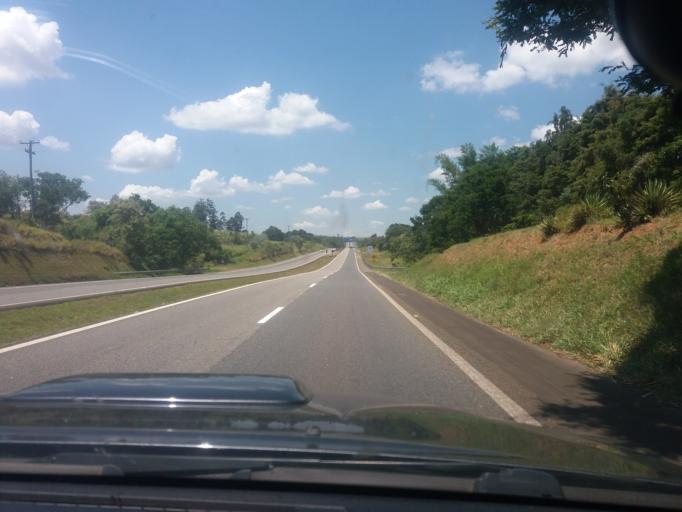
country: BR
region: Sao Paulo
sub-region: Tatui
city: Tatui
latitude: -23.4600
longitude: -47.9602
